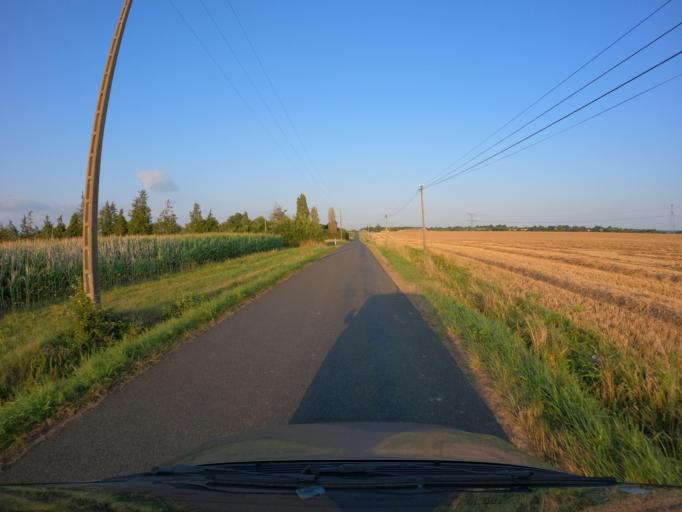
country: FR
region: Pays de la Loire
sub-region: Departement de la Sarthe
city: Parce-sur-Sarthe
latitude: 47.8765
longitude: -0.2142
